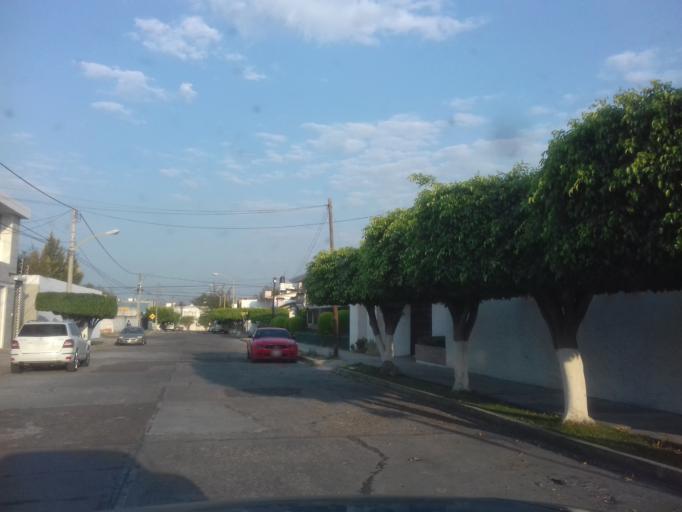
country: MX
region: Aguascalientes
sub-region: Aguascalientes
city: Aguascalientes
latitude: 21.8634
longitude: -102.2884
